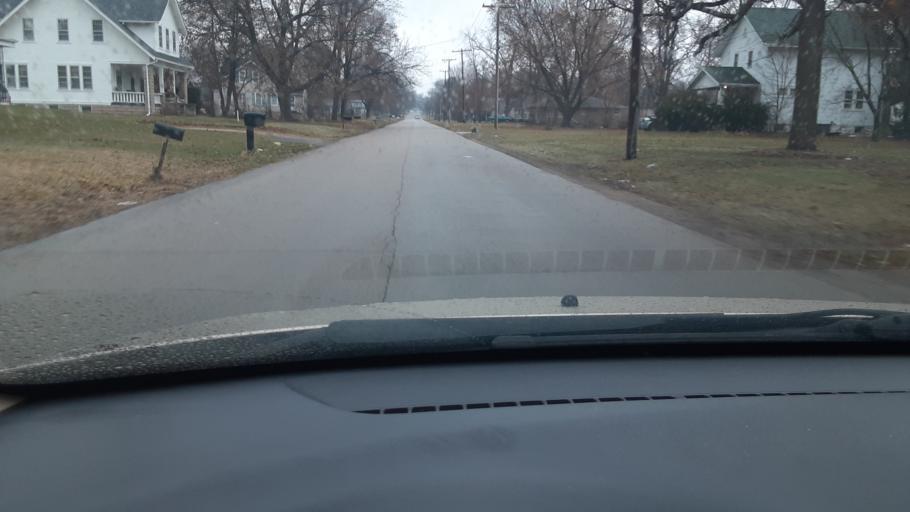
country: US
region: Illinois
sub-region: Winnebago County
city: Rockford
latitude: 42.3040
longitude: -89.1041
